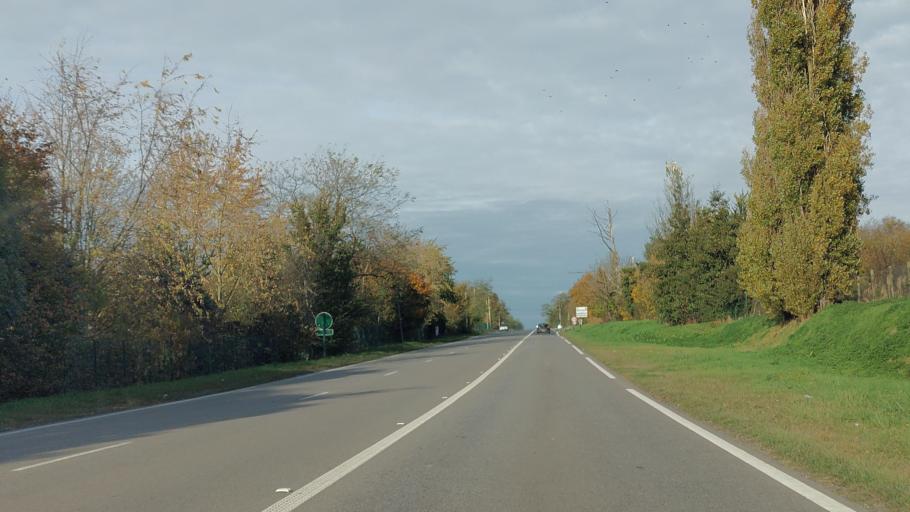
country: FR
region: Ile-de-France
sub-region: Departement du Val-d'Oise
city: Survilliers
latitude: 49.0880
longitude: 2.5302
